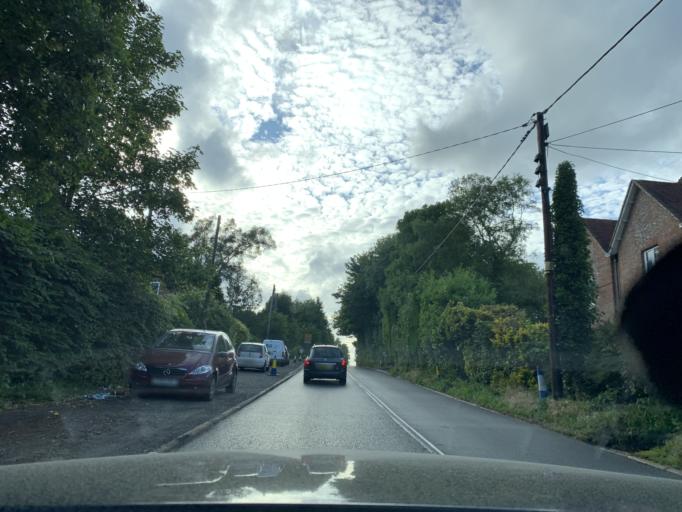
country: GB
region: England
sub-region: East Sussex
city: Robertsbridge
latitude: 50.9567
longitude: 0.4970
